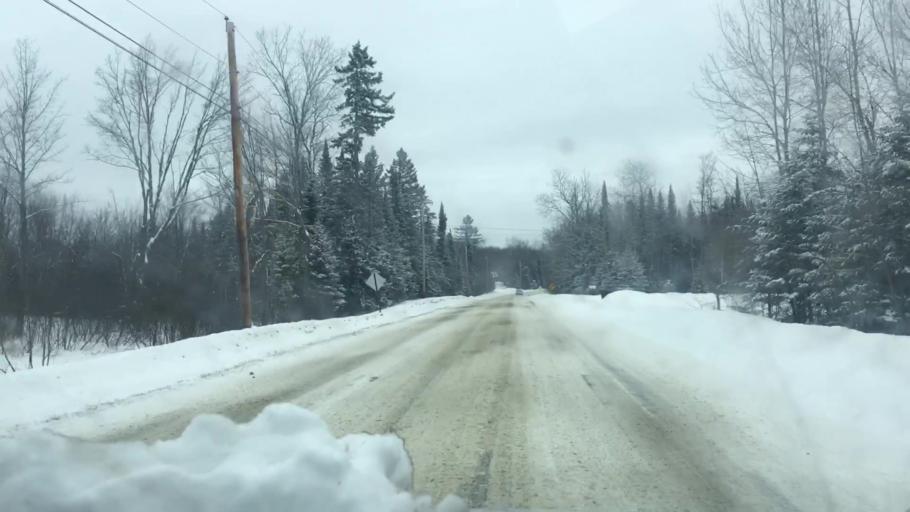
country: US
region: Maine
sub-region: Penobscot County
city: Bradford
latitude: 45.0319
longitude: -68.9525
